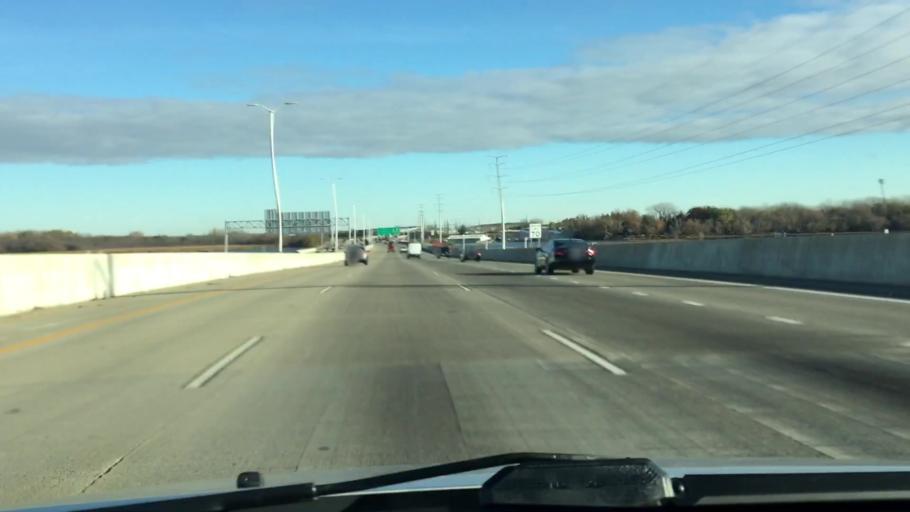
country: US
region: Wisconsin
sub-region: Winnebago County
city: Oshkosh
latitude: 44.0470
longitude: -88.5810
